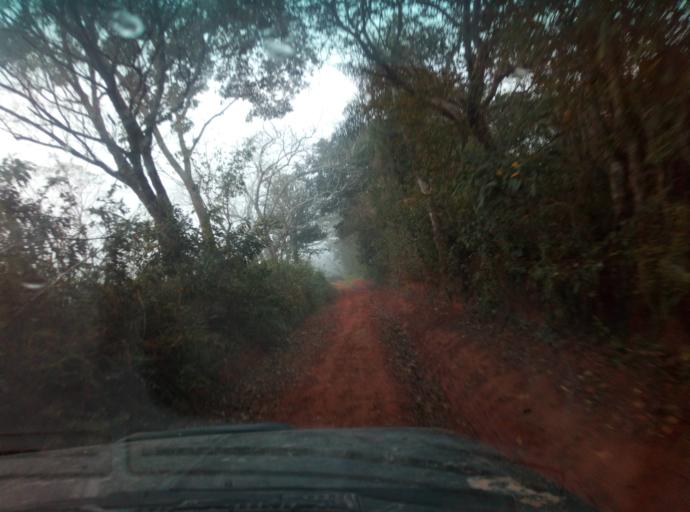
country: PY
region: Caaguazu
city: Doctor Cecilio Baez
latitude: -25.1514
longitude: -56.2520
